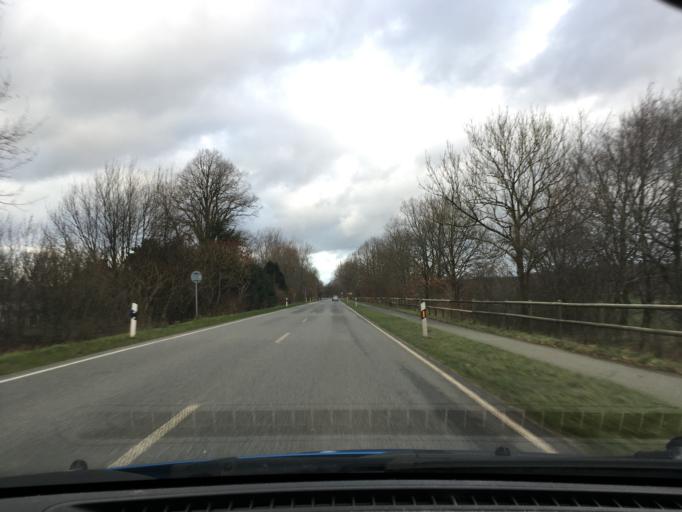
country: DE
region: Schleswig-Holstein
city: Kaisborstel
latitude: 53.9984
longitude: 9.4887
